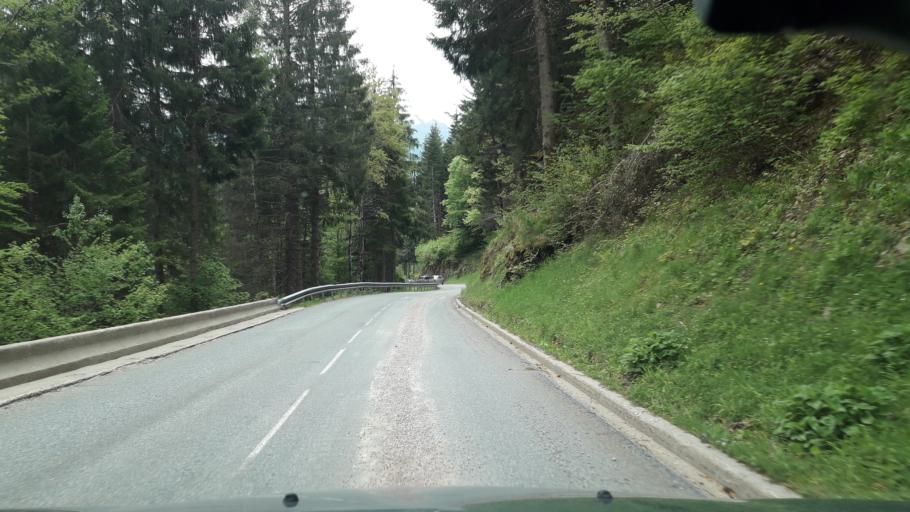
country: FR
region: Rhone-Alpes
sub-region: Departement de l'Isere
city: Huez
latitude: 45.1668
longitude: 6.0417
